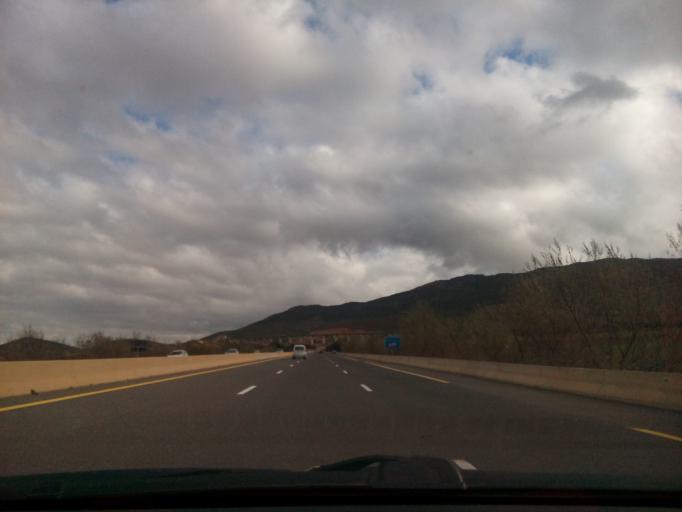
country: DZ
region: Tlemcen
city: Sidi Abdelli
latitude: 35.0097
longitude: -1.1750
